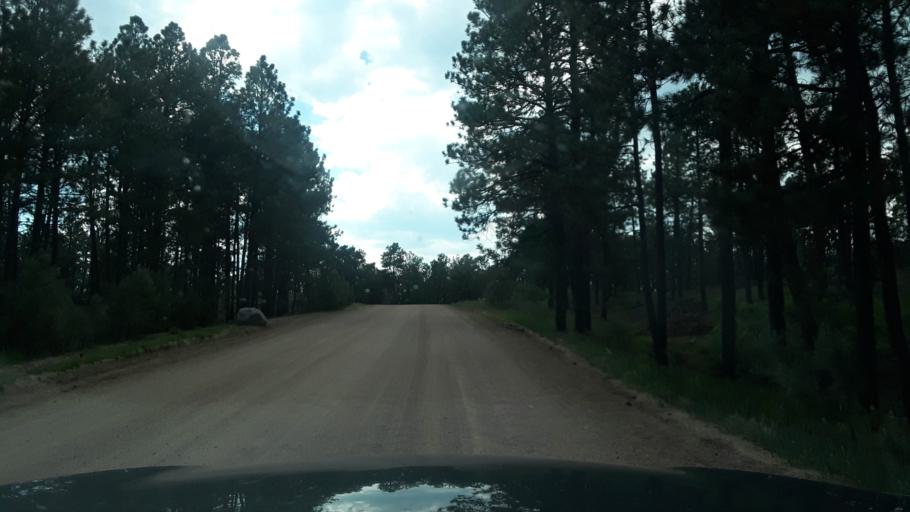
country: US
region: Colorado
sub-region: El Paso County
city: Gleneagle
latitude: 39.0600
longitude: -104.7892
